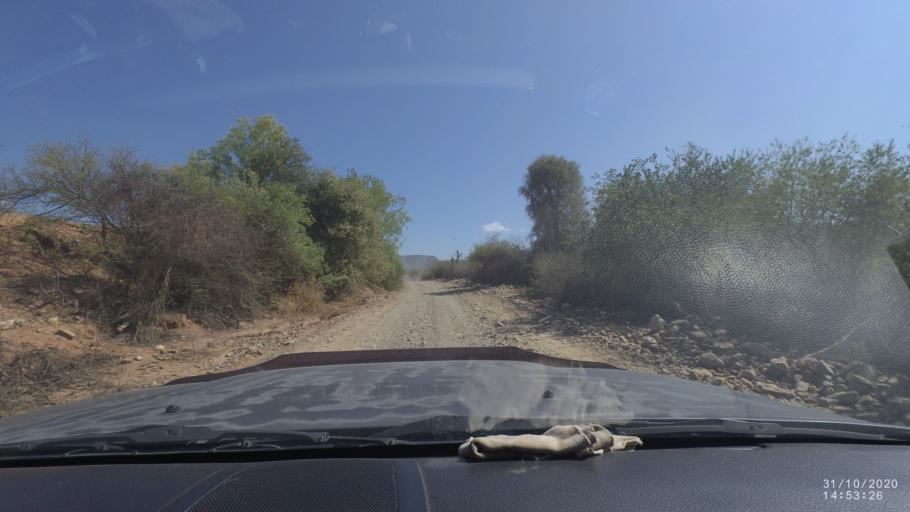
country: BO
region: Cochabamba
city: Aiquile
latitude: -18.2191
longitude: -64.8573
